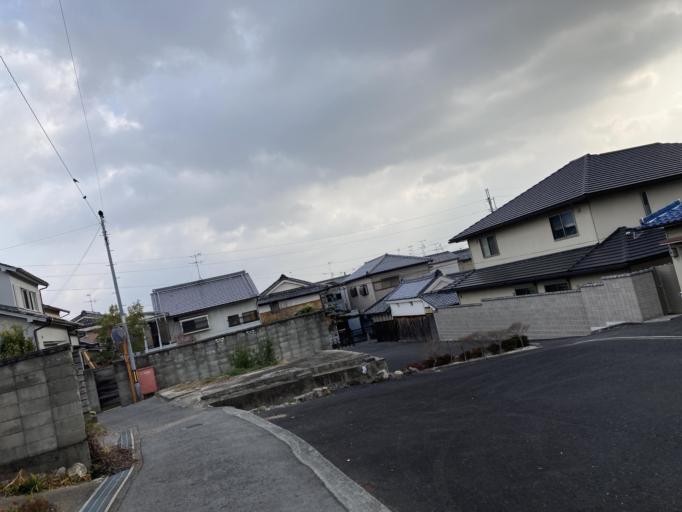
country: JP
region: Nara
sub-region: Ikoma-shi
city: Ikoma
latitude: 34.6083
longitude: 135.7210
